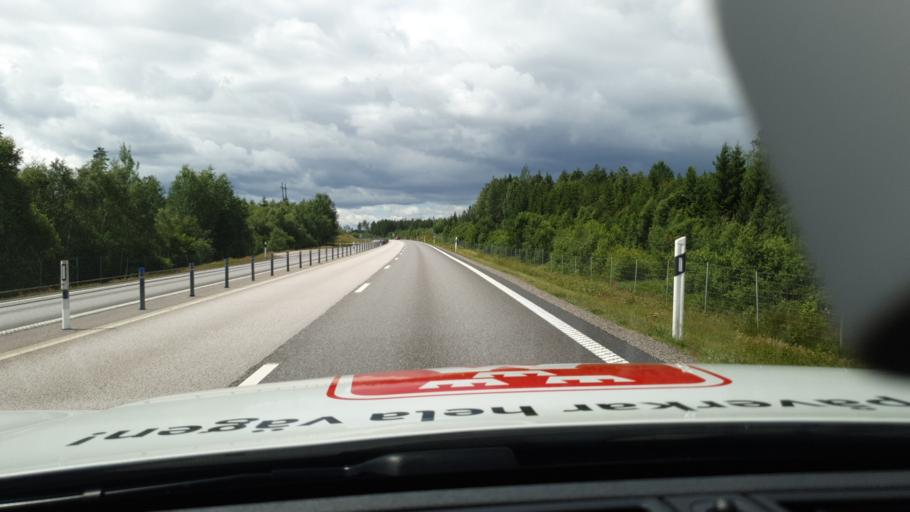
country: SE
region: Kronoberg
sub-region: Alvesta Kommun
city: Alvesta
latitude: 56.9220
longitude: 14.5427
